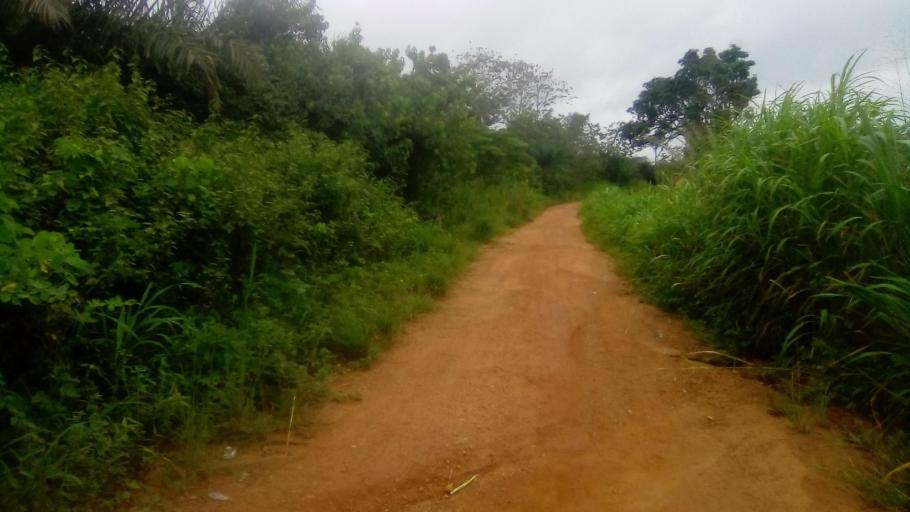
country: SL
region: Eastern Province
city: Kailahun
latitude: 8.2962
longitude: -10.5559
